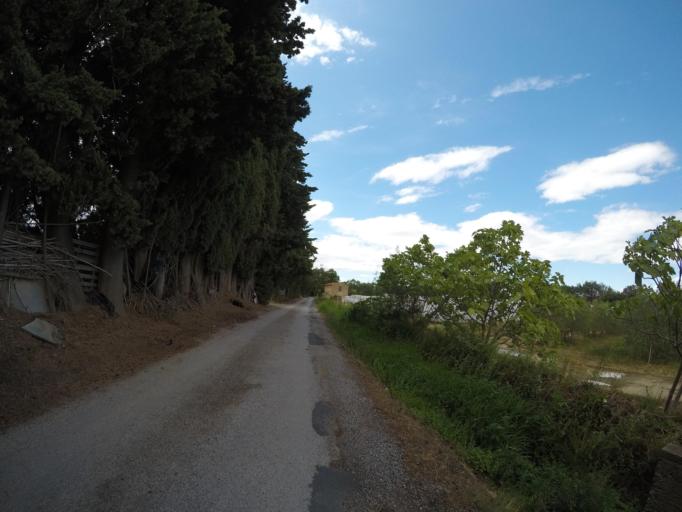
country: FR
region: Languedoc-Roussillon
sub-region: Departement des Pyrenees-Orientales
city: Pezilla-la-Riviere
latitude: 42.6997
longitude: 2.7855
